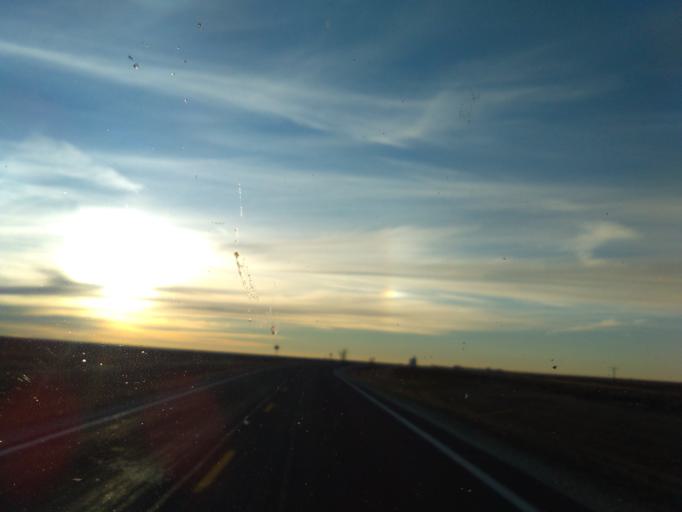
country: US
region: Kansas
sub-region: Logan County
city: Oakley
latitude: 39.0951
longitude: -101.1101
